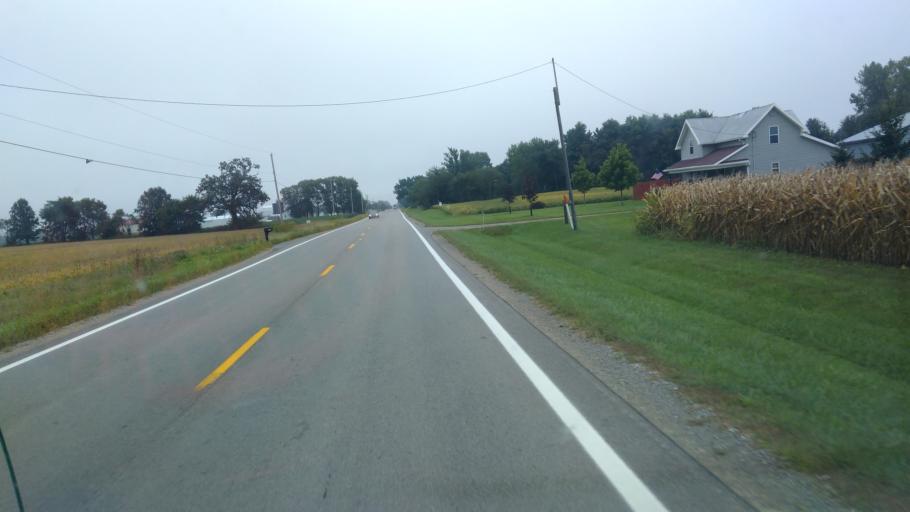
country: US
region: Ohio
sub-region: Union County
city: Richwood
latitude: 40.4782
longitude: -83.4759
